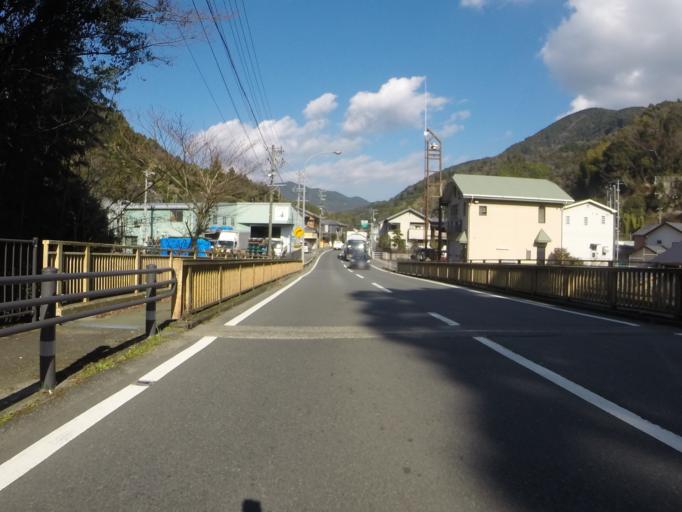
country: JP
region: Shizuoka
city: Fujinomiya
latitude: 35.1067
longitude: 138.5131
